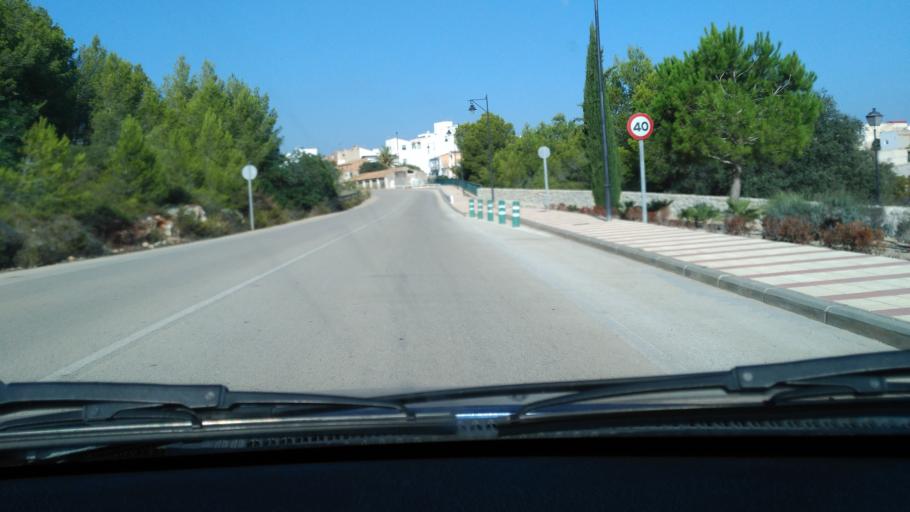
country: ES
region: Valencia
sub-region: Provincia de Alicante
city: Gata de Gorgos
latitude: 38.7706
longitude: 0.0867
